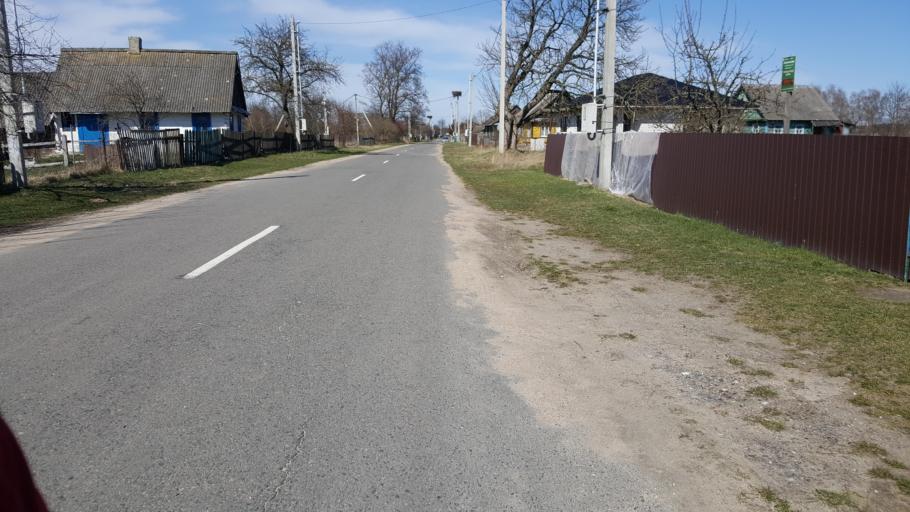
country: BY
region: Brest
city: Charnawchytsy
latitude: 52.3043
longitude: 23.7793
